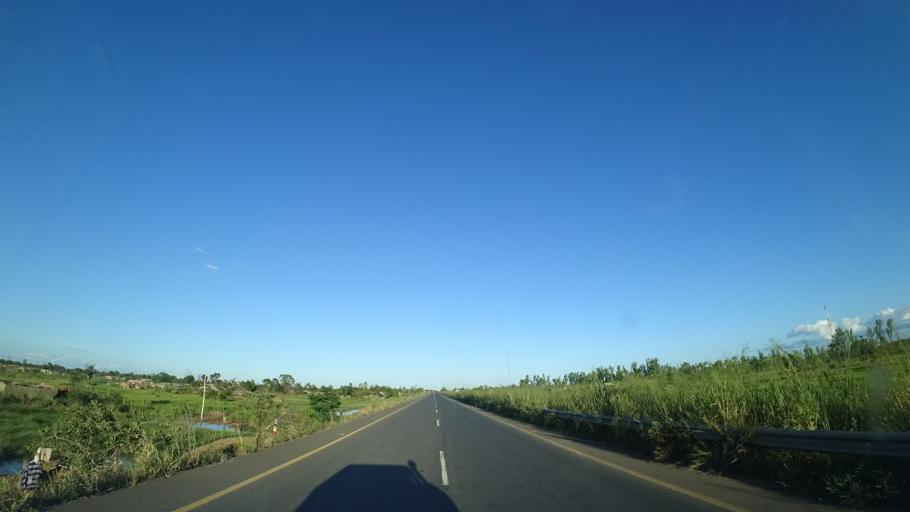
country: MZ
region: Sofala
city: Dondo
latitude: -19.3292
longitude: 34.3113
